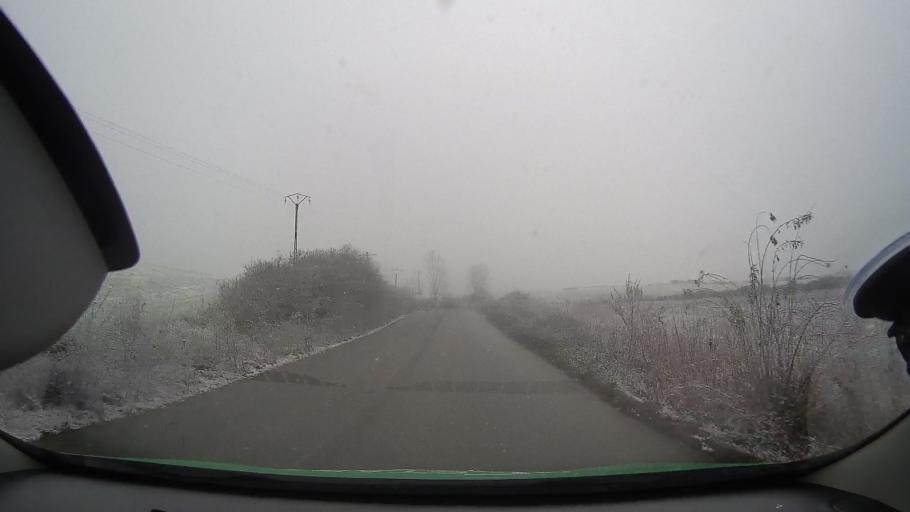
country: RO
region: Alba
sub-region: Comuna Noslac
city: Noslac
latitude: 46.3762
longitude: 23.9108
